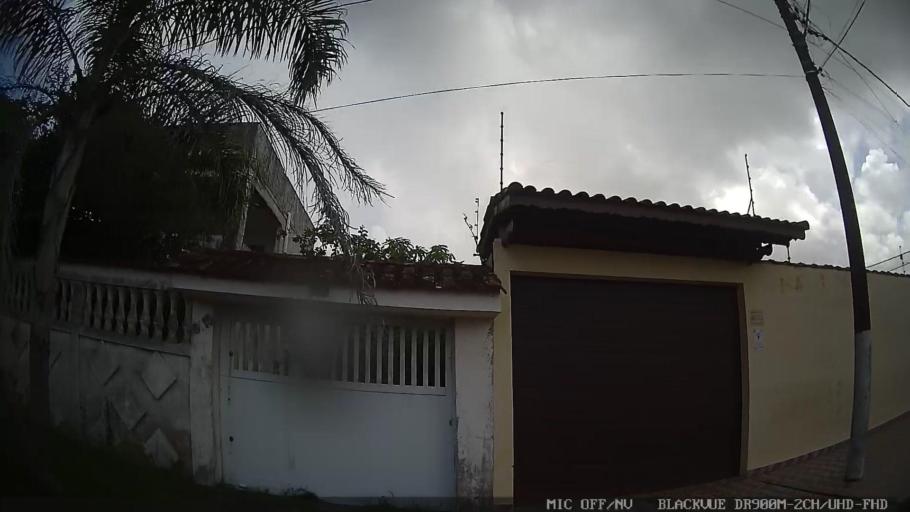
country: BR
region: Sao Paulo
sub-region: Itanhaem
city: Itanhaem
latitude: -24.1585
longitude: -46.7344
